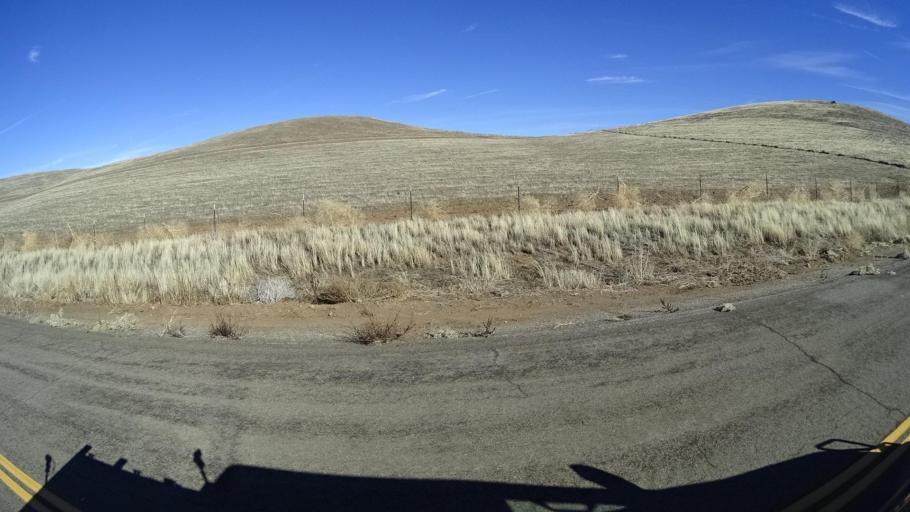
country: US
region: California
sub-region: Kern County
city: Maricopa
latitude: 34.9135
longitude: -119.4006
